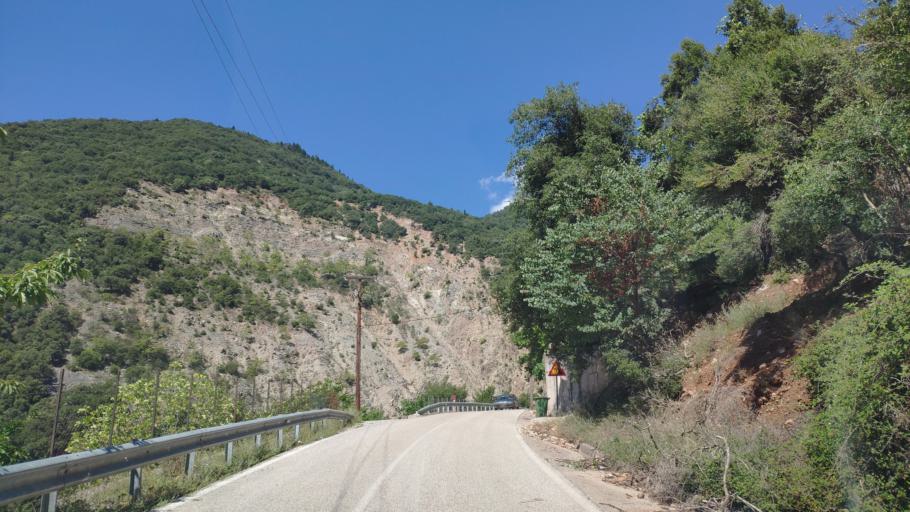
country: GR
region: Central Greece
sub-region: Nomos Evrytanias
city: Kerasochori
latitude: 39.0385
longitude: 21.5969
